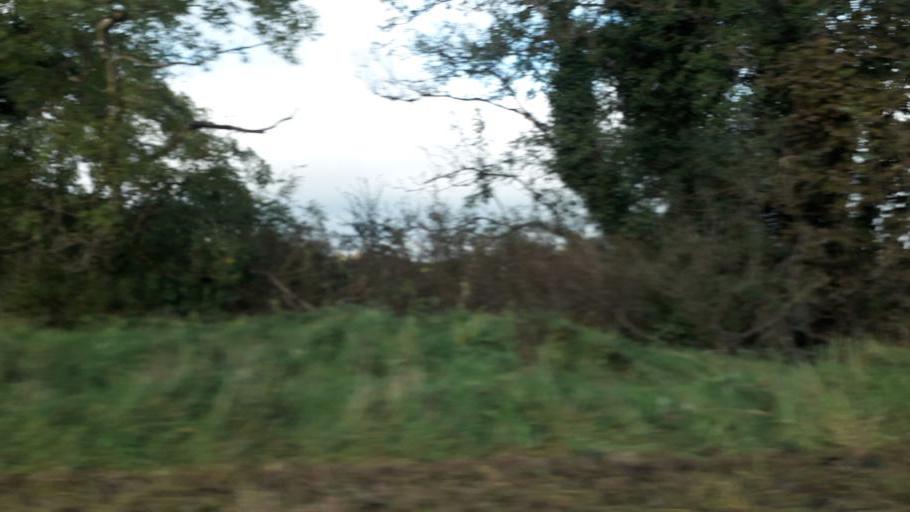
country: IE
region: Connaught
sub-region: Roscommon
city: Castlerea
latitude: 53.8792
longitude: -8.4364
